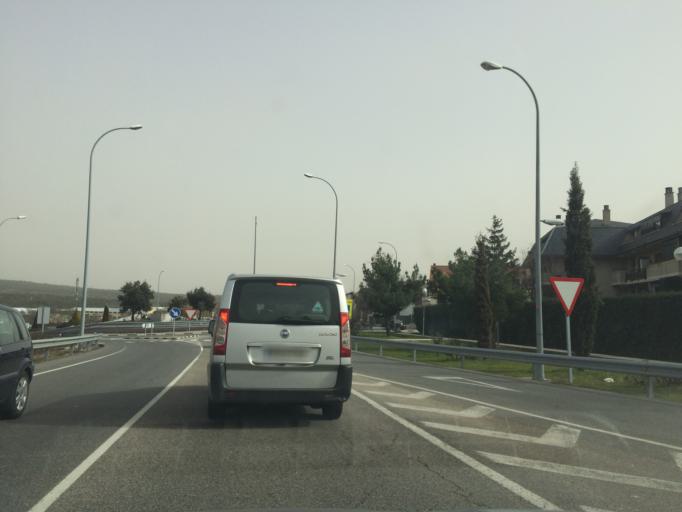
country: ES
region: Madrid
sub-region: Provincia de Madrid
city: Boalo
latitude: 40.6996
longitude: -3.9325
